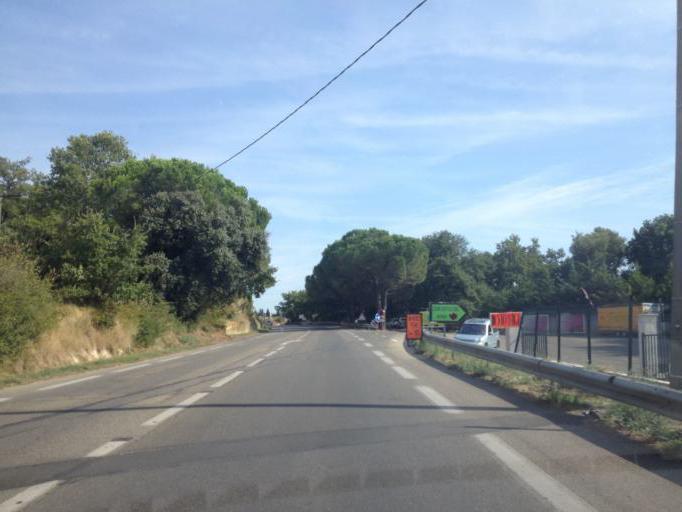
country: FR
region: Provence-Alpes-Cote d'Azur
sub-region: Departement du Vaucluse
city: Aubignan
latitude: 44.0839
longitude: 5.0353
